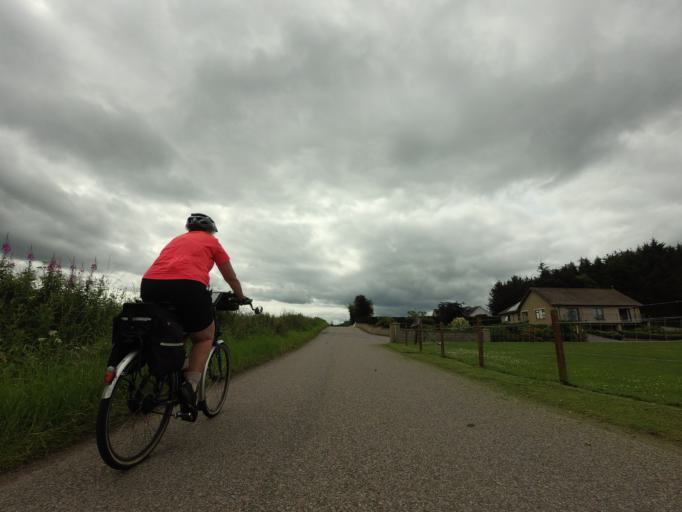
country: GB
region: Scotland
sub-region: Moray
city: Forres
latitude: 57.6003
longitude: -3.6959
